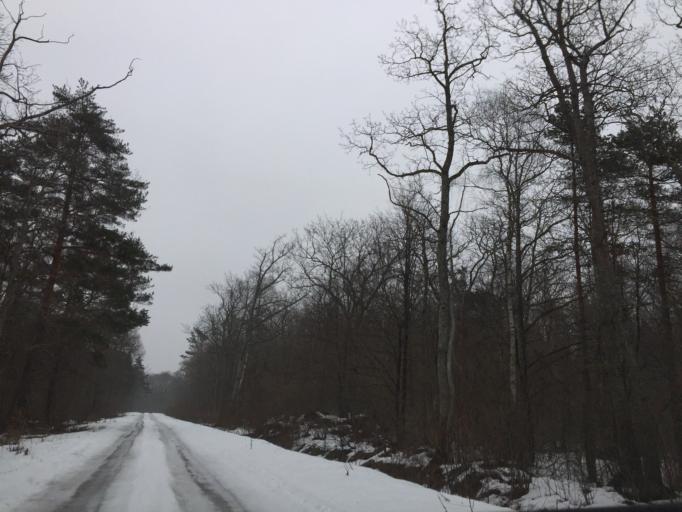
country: EE
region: Saare
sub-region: Kuressaare linn
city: Kuressaare
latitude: 58.2731
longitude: 22.5630
